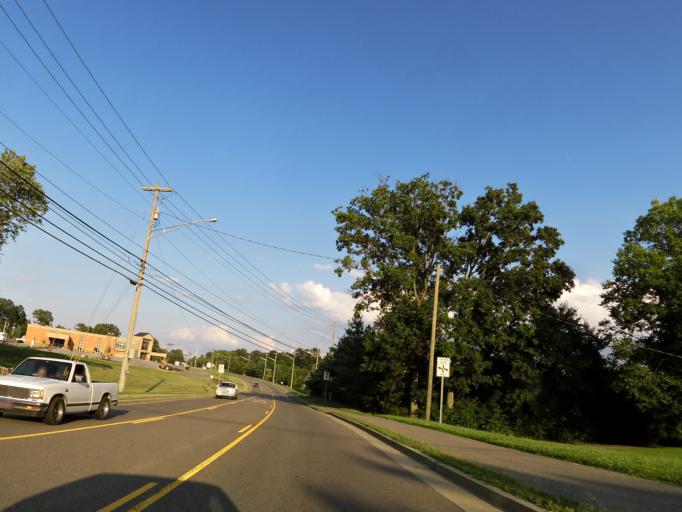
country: US
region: Tennessee
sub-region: Knox County
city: Knoxville
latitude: 35.9879
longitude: -83.9966
